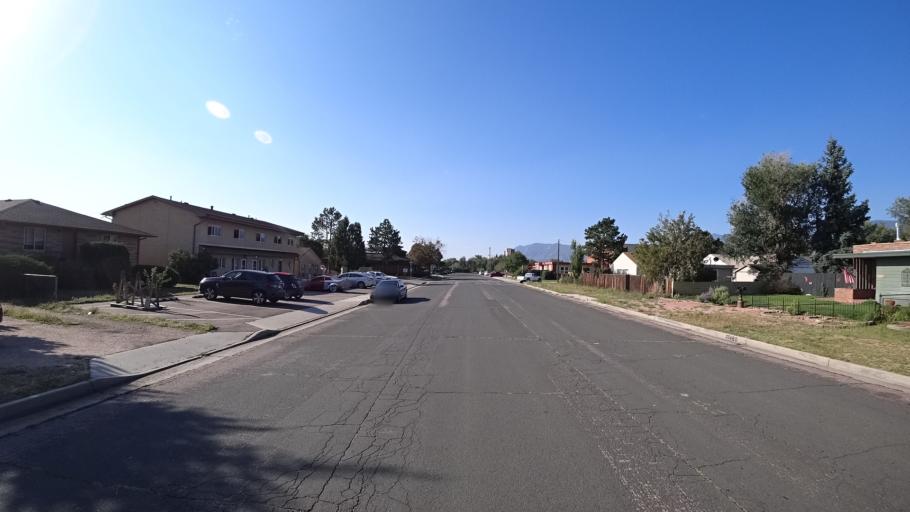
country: US
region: Colorado
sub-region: El Paso County
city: Colorado Springs
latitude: 38.8725
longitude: -104.8215
